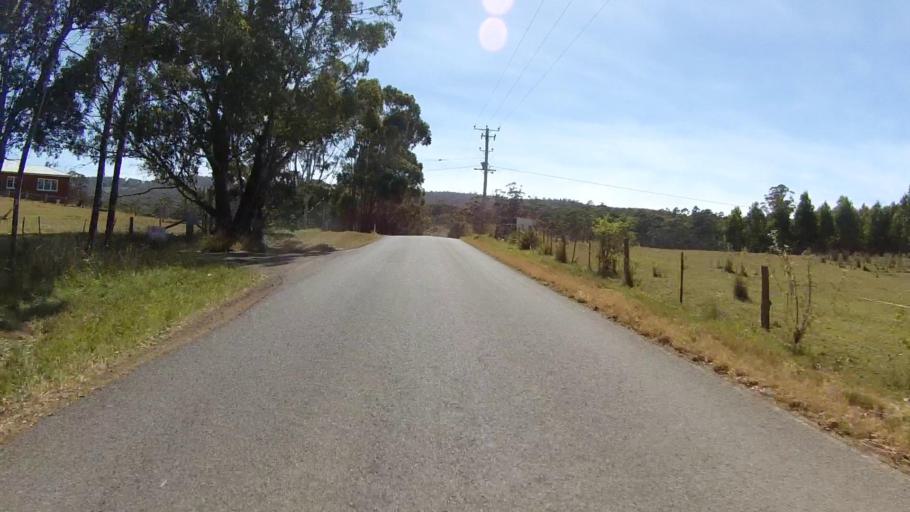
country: AU
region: Tasmania
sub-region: Sorell
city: Sorell
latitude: -42.7495
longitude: 147.7175
